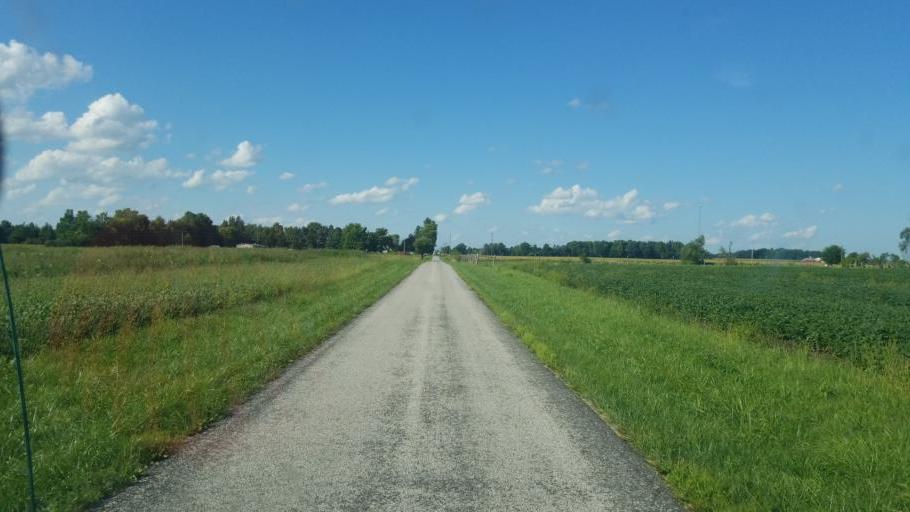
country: US
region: Ohio
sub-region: Marion County
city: Marion
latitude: 40.6197
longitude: -83.2694
